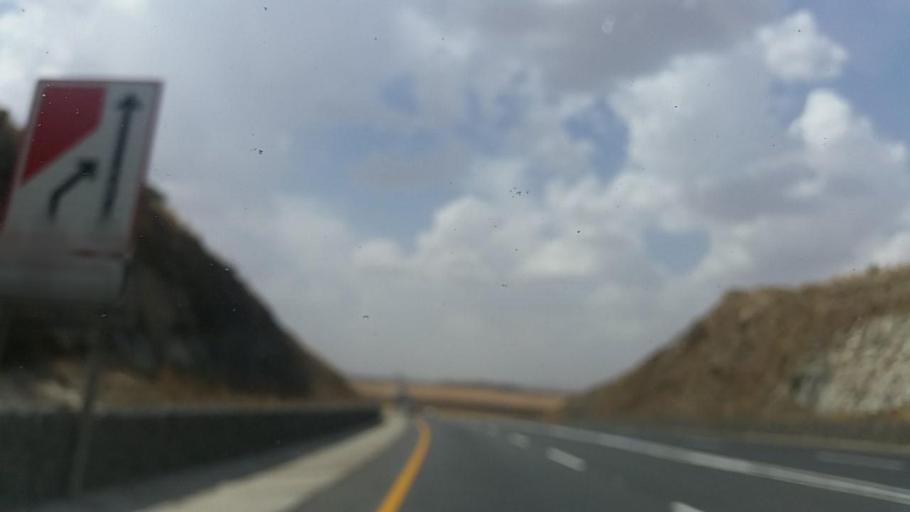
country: ZA
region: Orange Free State
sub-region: Xhariep District Municipality
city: Trompsburg
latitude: -30.3997
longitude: 25.6715
